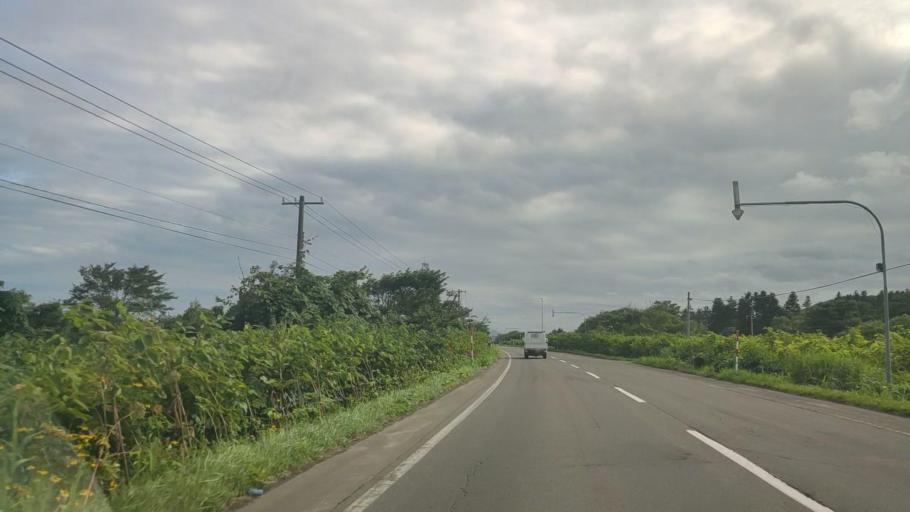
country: JP
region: Hokkaido
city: Niseko Town
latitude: 42.4591
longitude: 140.3353
